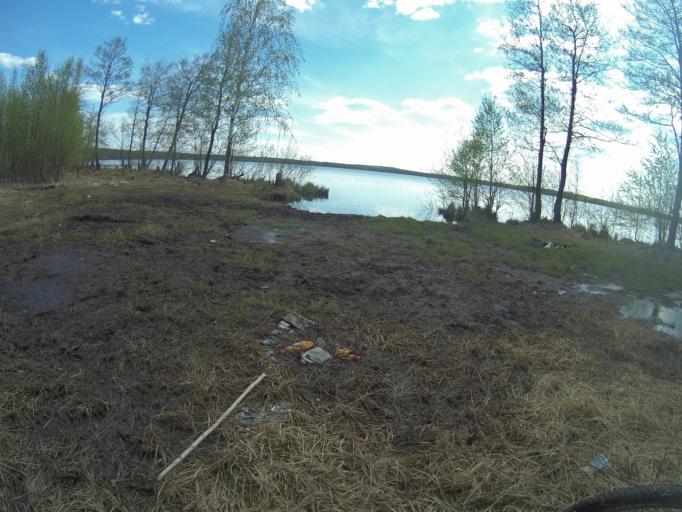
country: RU
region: Vladimir
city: Vorsha
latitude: 55.9475
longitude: 40.1928
